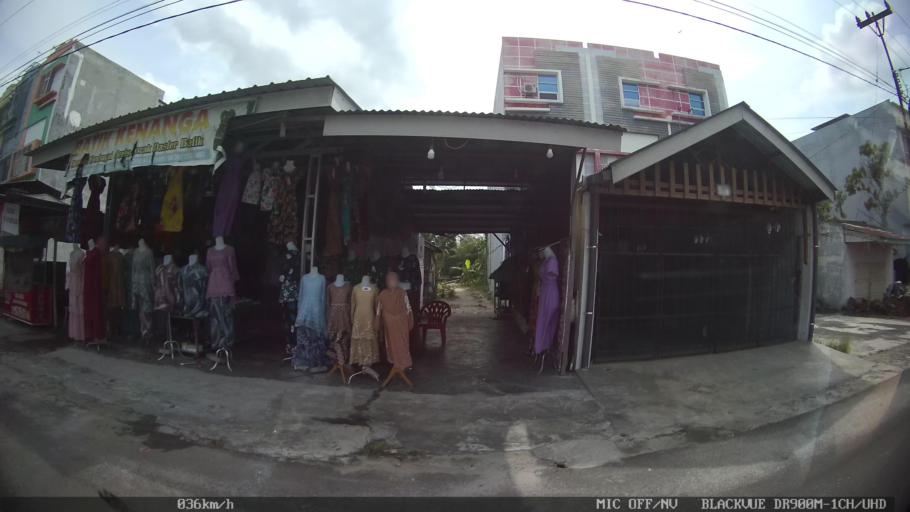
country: ID
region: North Sumatra
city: Percut
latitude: 3.5788
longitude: 98.8645
